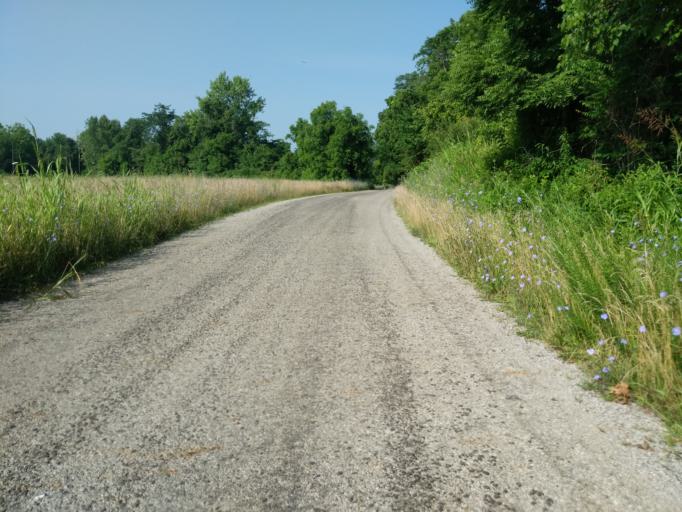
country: US
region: Ohio
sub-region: Athens County
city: Athens
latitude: 39.3444
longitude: -82.1147
